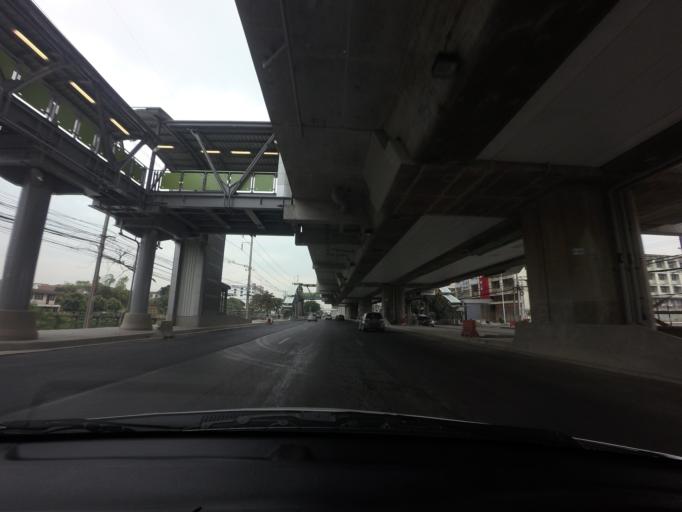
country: TH
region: Samut Prakan
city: Samut Prakan
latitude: 13.5681
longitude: 100.6076
